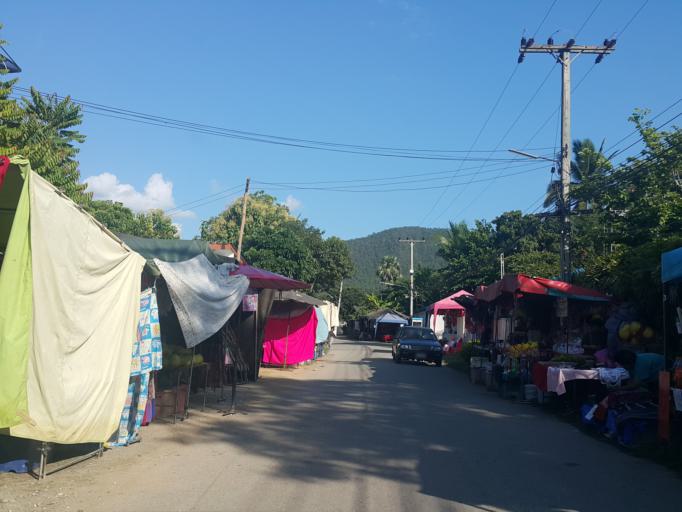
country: TH
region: Chiang Mai
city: Mae On
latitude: 18.7204
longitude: 99.2096
